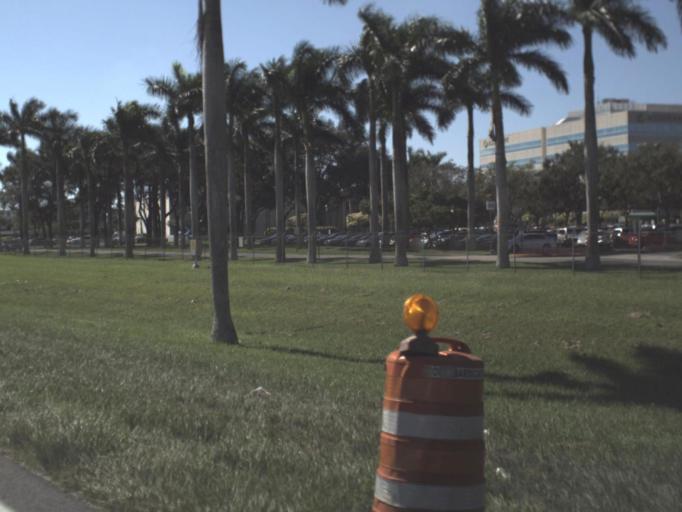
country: US
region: Florida
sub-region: Miami-Dade County
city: South Miami Heights
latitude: 25.5886
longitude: -80.3687
